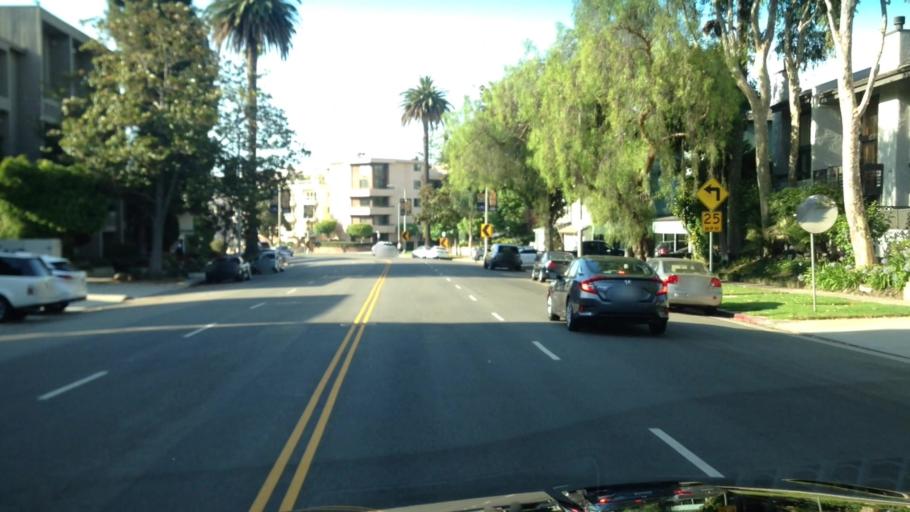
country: US
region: California
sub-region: Los Angeles County
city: Century City
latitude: 34.0545
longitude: -118.4231
